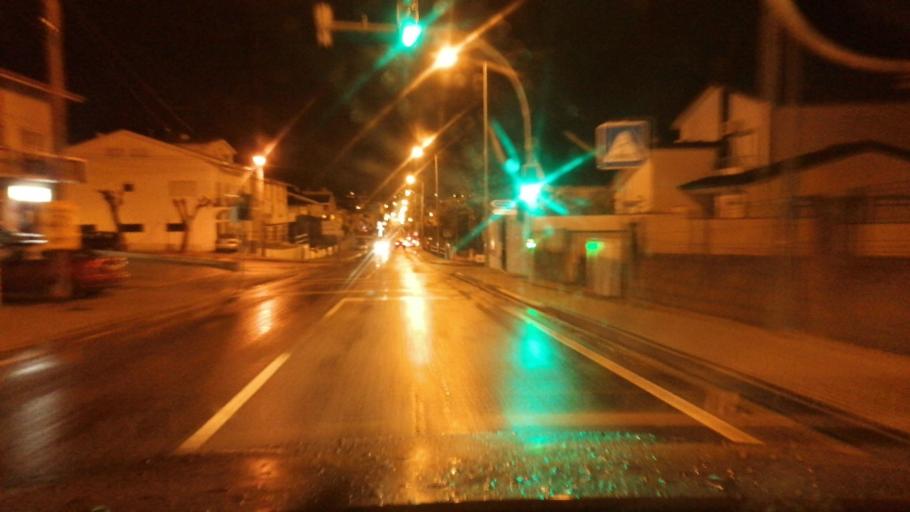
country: PT
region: Viseu
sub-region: Moimenta da Beira
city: Moimenta da Beira
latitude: 40.9740
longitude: -7.6083
